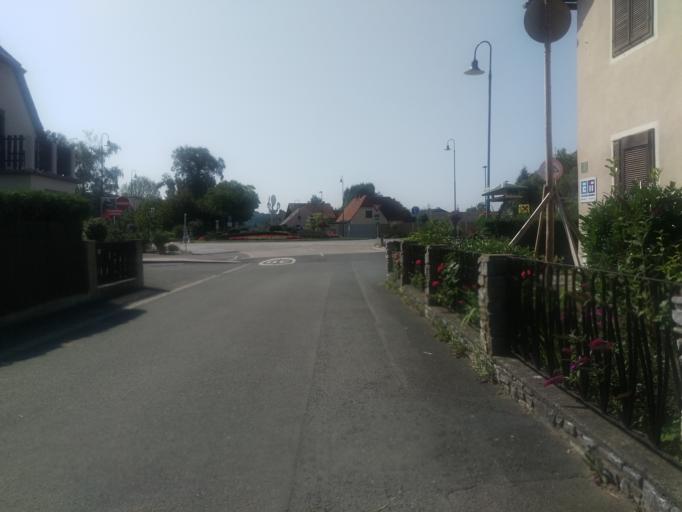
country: AT
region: Styria
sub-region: Politischer Bezirk Graz-Umgebung
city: Fernitz
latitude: 46.9729
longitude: 15.4976
